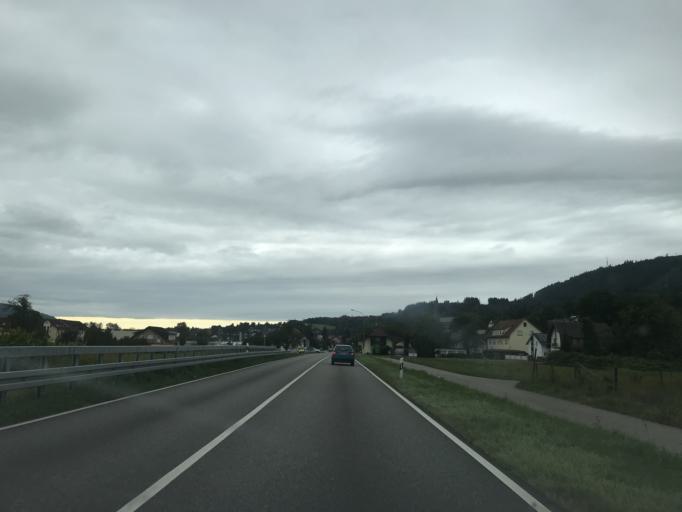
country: CH
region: Aargau
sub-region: Bezirk Laufenburg
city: Eiken
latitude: 47.5596
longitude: 7.9772
